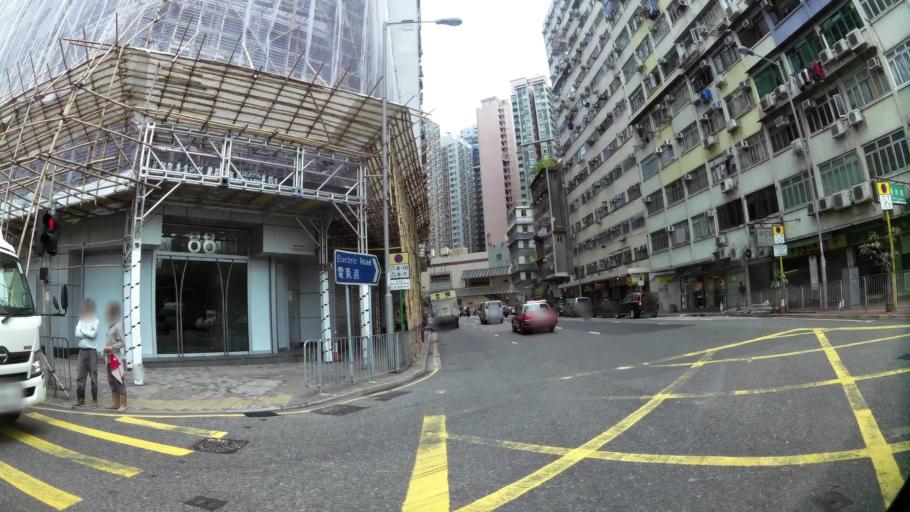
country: HK
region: Wanchai
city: Wan Chai
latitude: 22.2856
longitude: 114.1906
